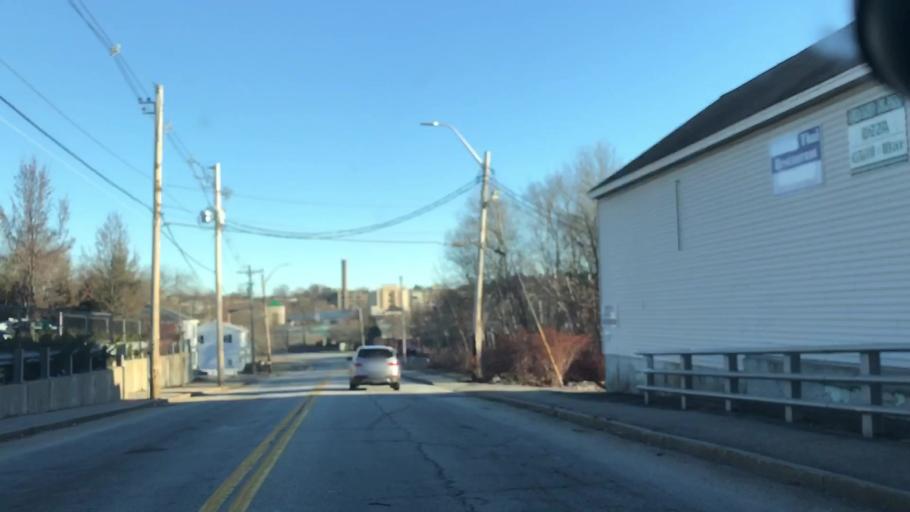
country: US
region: New Hampshire
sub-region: Hillsborough County
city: Manchester
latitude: 42.9761
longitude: -71.4792
